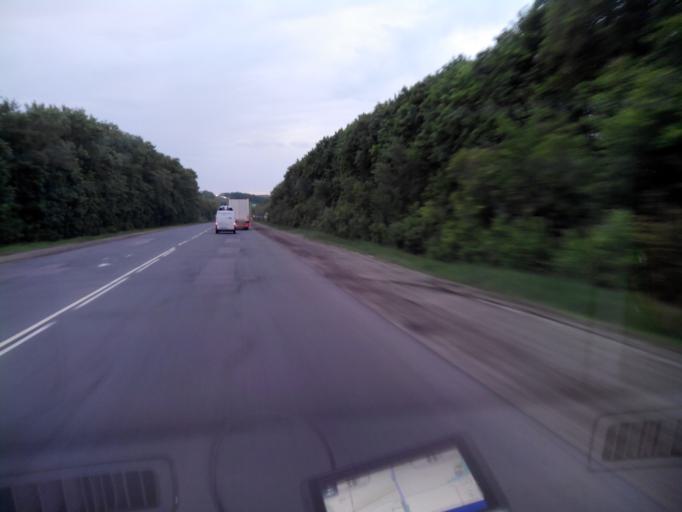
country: RU
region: Penza
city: Chemodanovka
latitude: 53.2274
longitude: 45.3513
